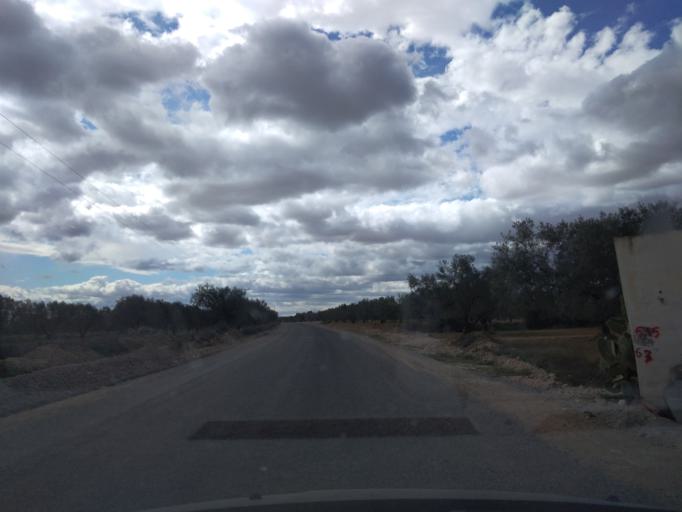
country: TN
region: Susah
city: Akouda
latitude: 35.8118
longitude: 10.4462
